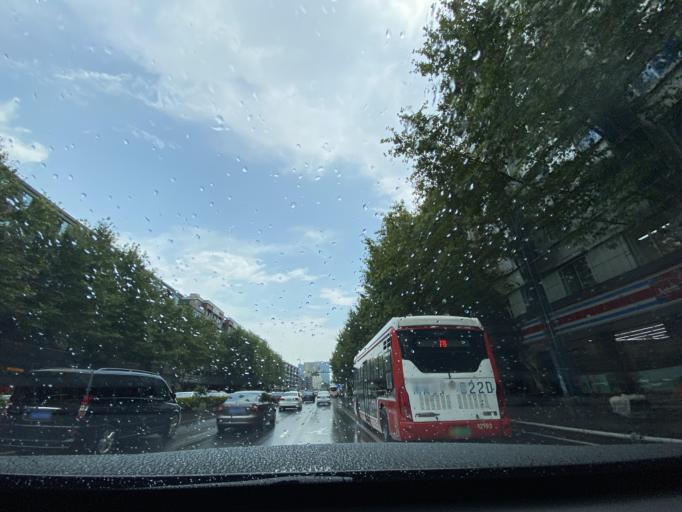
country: CN
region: Sichuan
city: Chengdu
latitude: 30.6431
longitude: 104.0732
